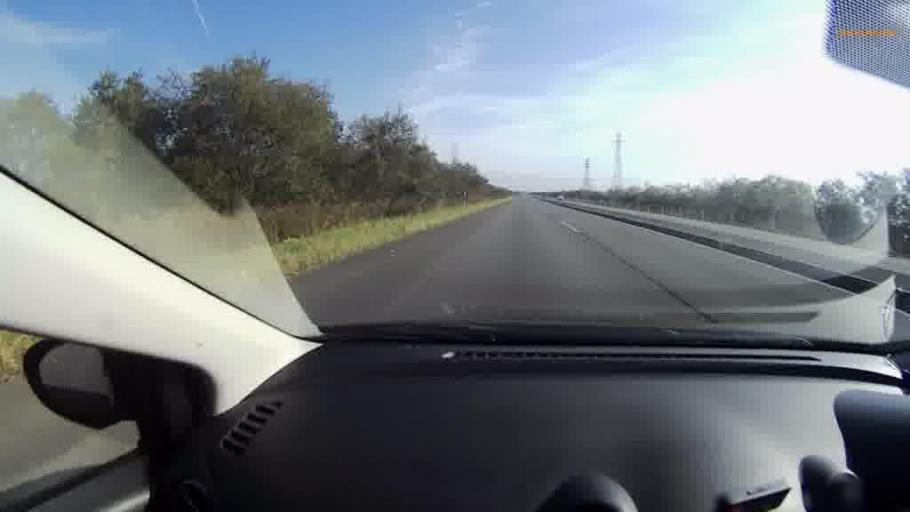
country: JP
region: Hokkaido
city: Kushiro
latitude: 43.0274
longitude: 144.2925
